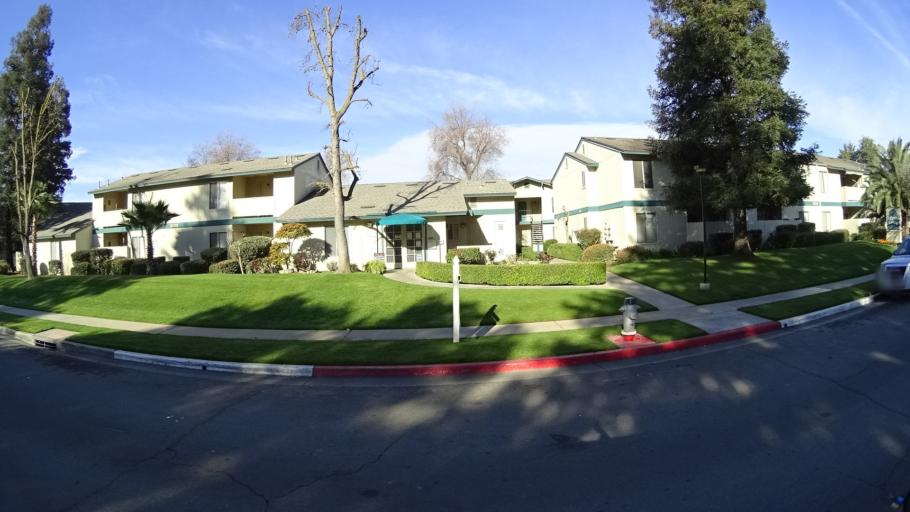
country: US
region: California
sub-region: Fresno County
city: West Park
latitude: 36.8201
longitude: -119.8580
